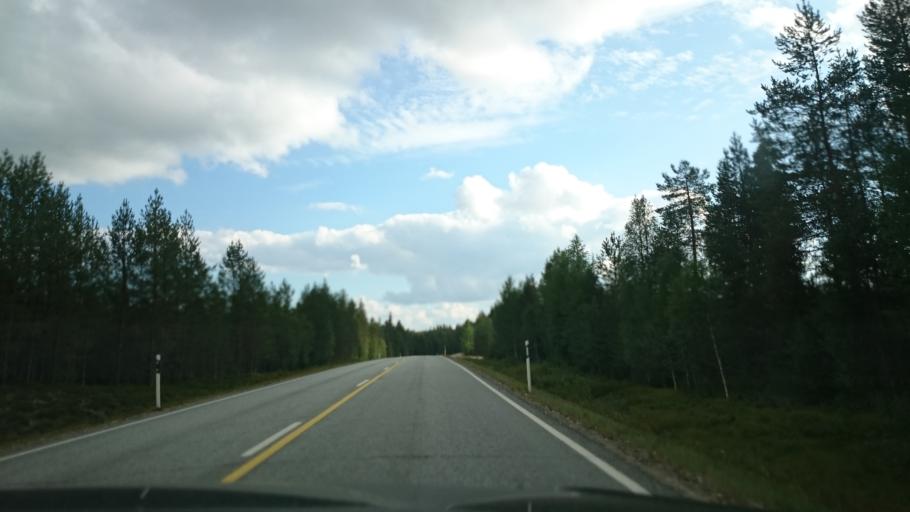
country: FI
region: Kainuu
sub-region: Kehys-Kainuu
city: Kuhmo
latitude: 64.5220
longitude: 29.9460
